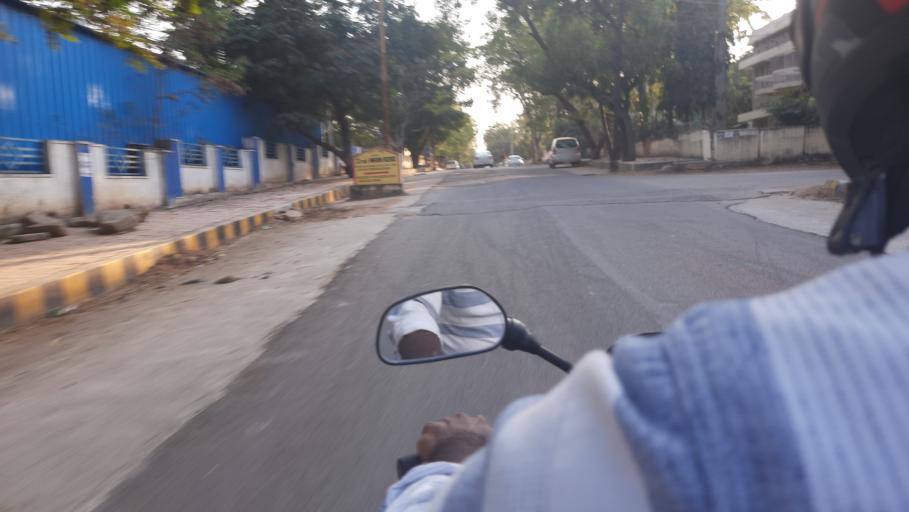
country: IN
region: Telangana
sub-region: Rangareddi
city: Secunderabad
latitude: 17.4872
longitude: 78.5482
